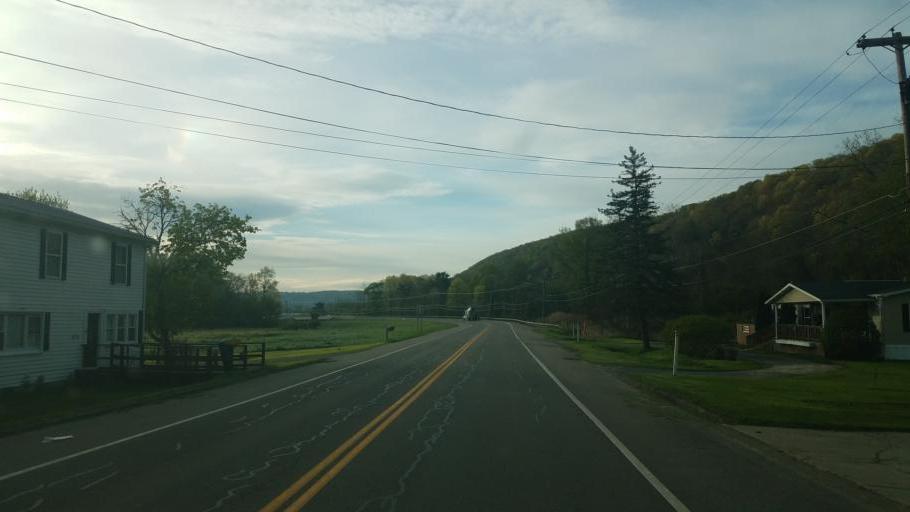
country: US
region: New York
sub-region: Steuben County
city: Hornell
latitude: 42.3361
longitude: -77.6860
